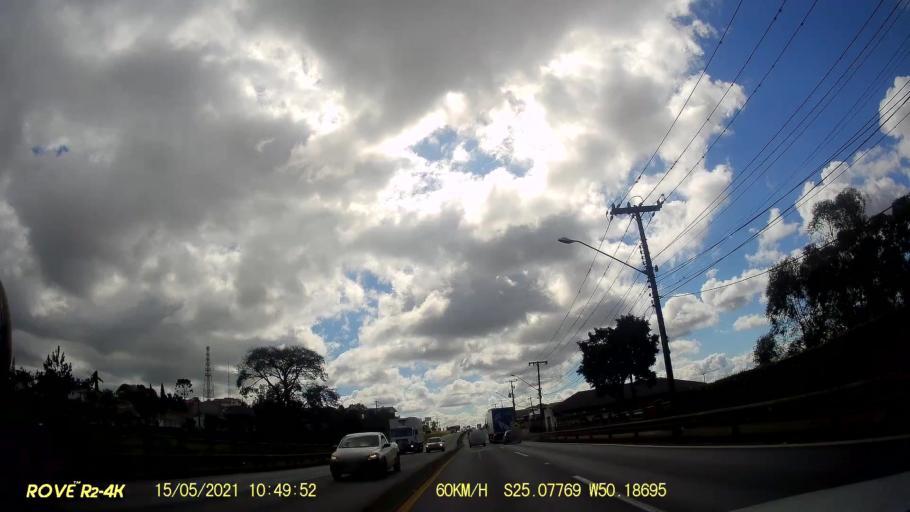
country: BR
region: Parana
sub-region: Ponta Grossa
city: Ponta Grossa
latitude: -25.0776
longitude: -50.1869
